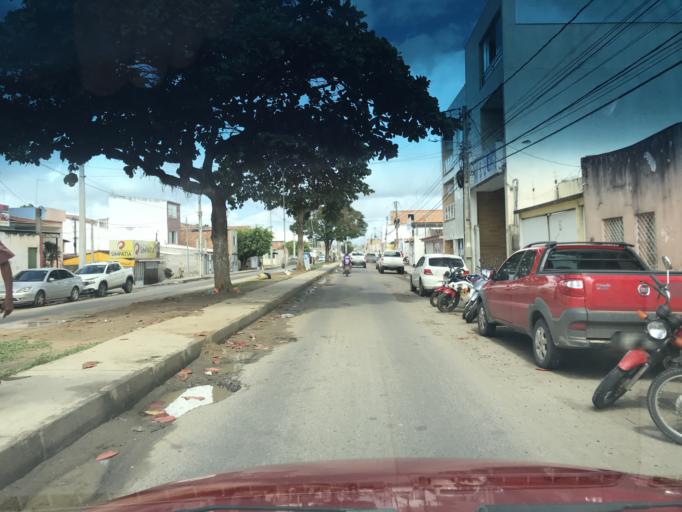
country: BR
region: Bahia
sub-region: Santo Antonio De Jesus
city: Santo Antonio de Jesus
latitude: -12.9690
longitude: -39.2711
